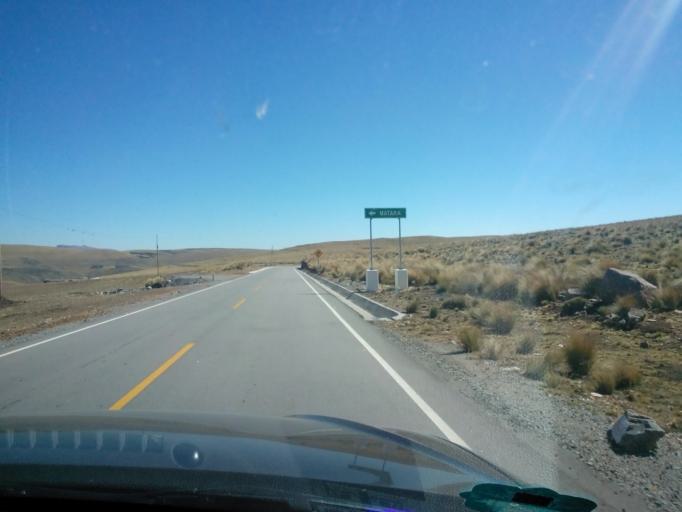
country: PE
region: Ayacucho
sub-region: Provincia de Huamanga
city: Ocros
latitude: -13.3947
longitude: -73.9597
